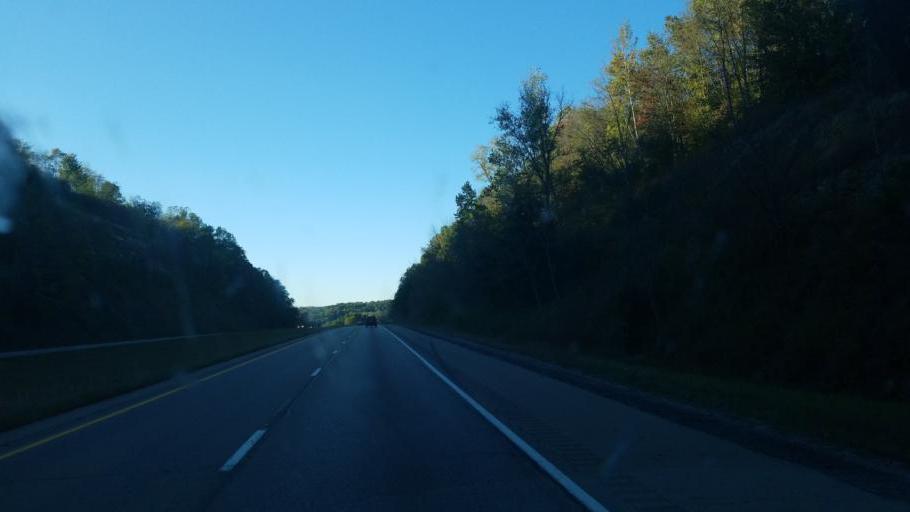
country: US
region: Ohio
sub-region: Tuscarawas County
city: Newcomerstown
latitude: 40.1706
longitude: -81.5488
